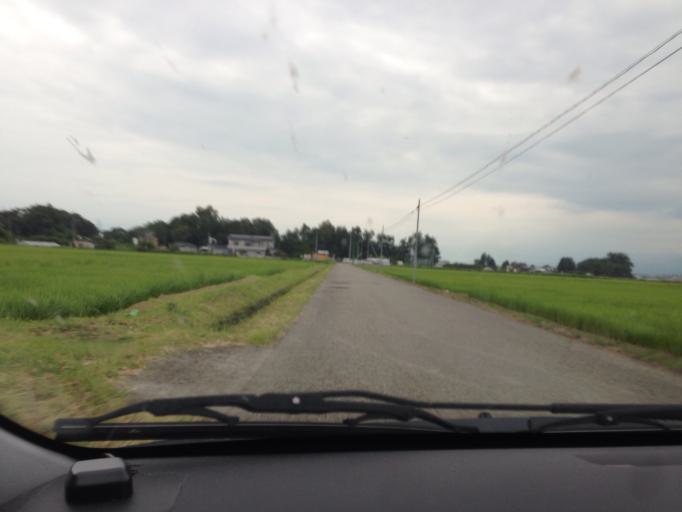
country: JP
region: Fukushima
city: Kitakata
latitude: 37.5076
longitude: 139.8945
